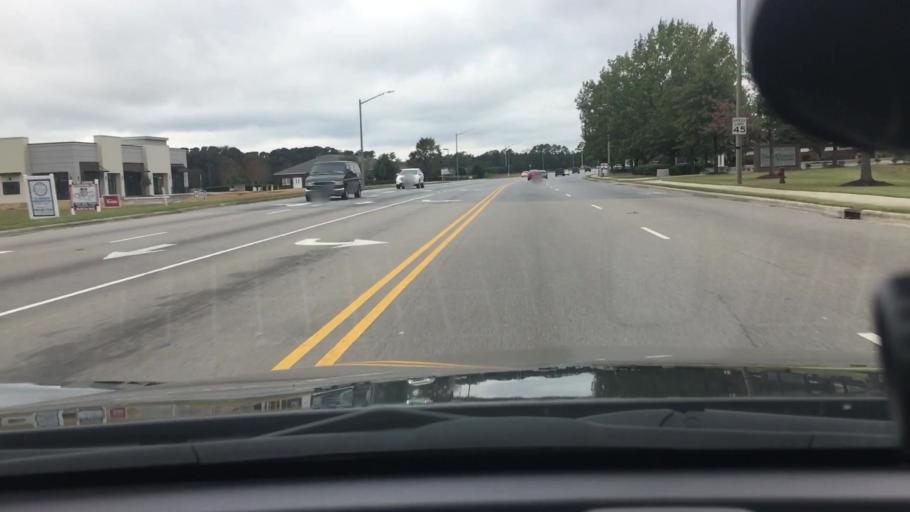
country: US
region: North Carolina
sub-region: Pitt County
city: Summerfield
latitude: 35.5953
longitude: -77.4029
